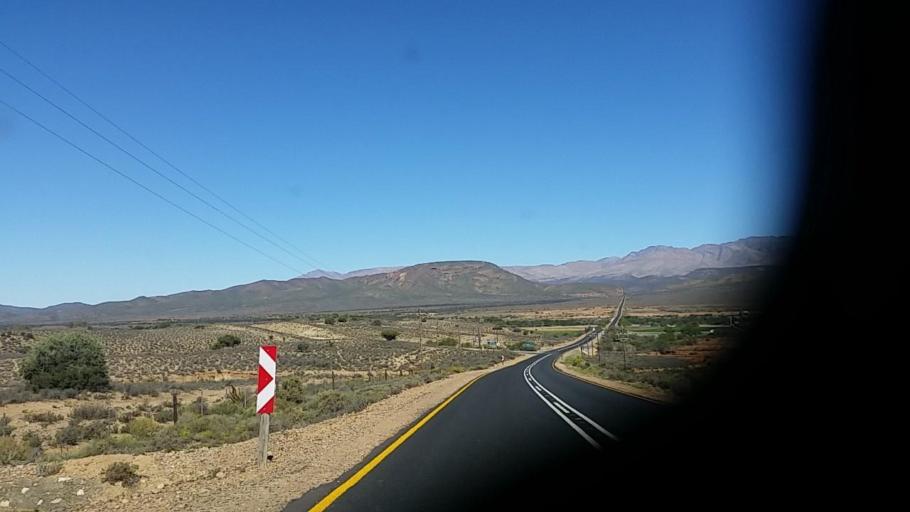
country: ZA
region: Western Cape
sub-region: Eden District Municipality
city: Oudtshoorn
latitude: -33.5001
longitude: 22.6846
